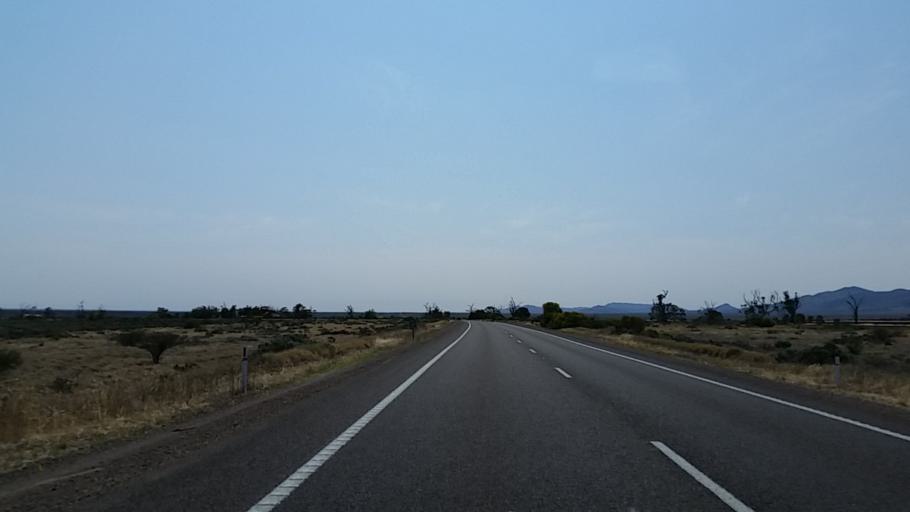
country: AU
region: South Australia
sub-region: Port Augusta
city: Port Augusta
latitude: -32.6941
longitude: 137.9418
